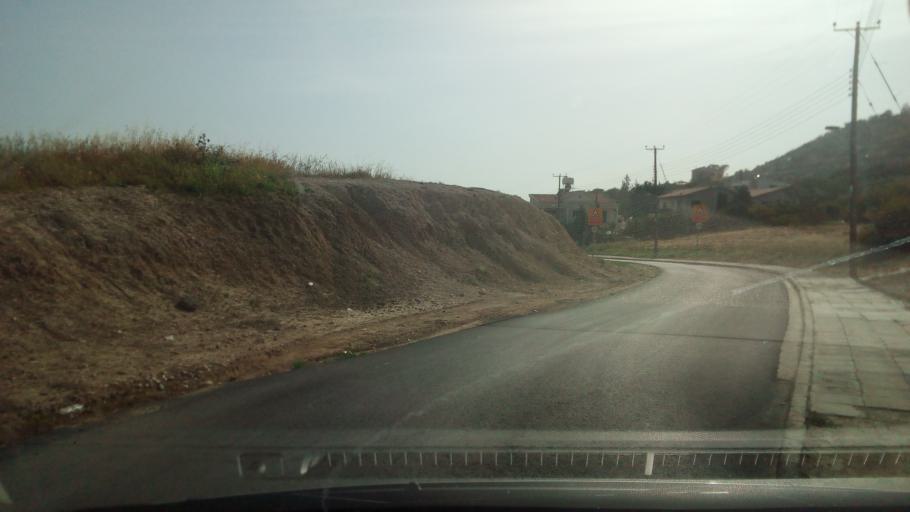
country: CY
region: Larnaka
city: Voroklini
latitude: 34.9809
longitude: 33.6516
